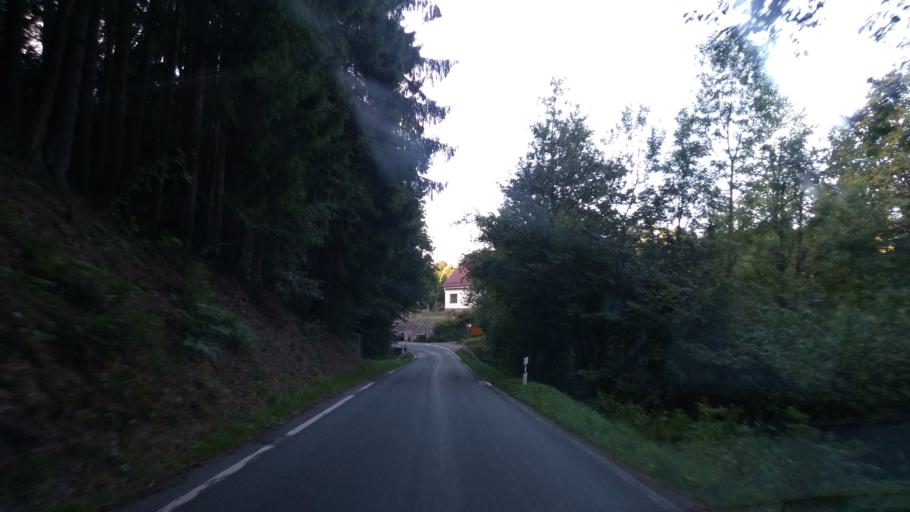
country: DE
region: North Rhine-Westphalia
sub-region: Regierungsbezirk Koln
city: Gummersbach
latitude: 51.0283
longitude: 7.5278
